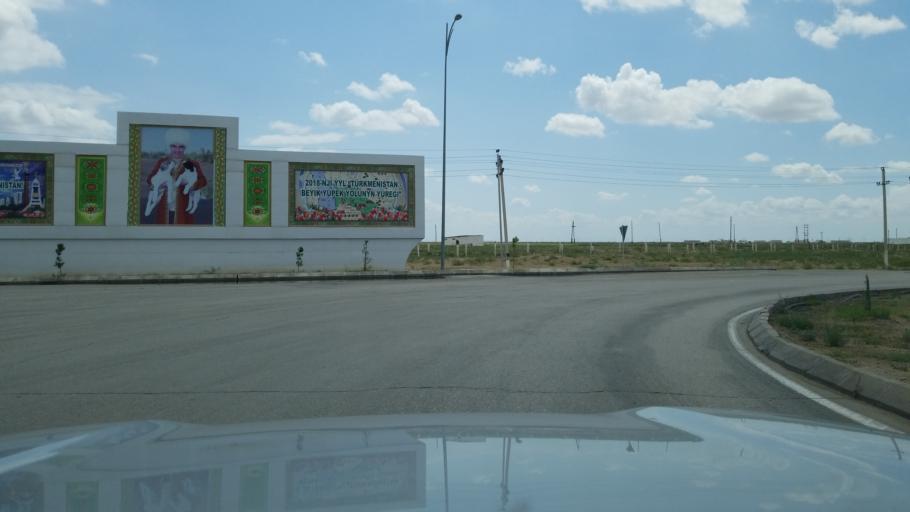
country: TM
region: Balkan
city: Balkanabat
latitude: 39.4867
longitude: 54.3742
